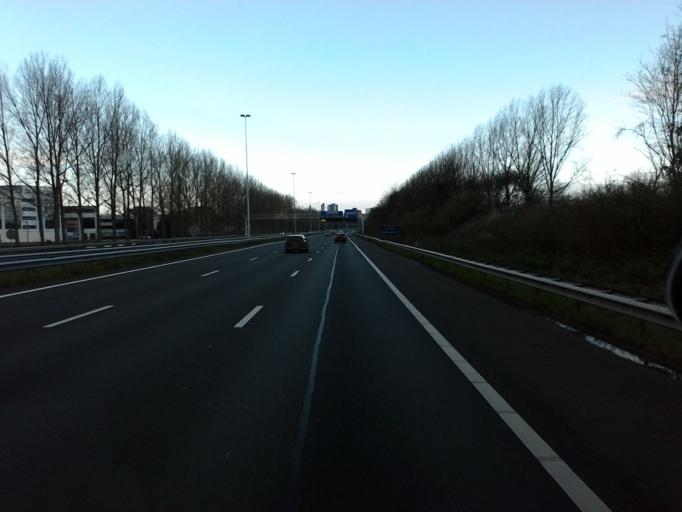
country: NL
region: South Holland
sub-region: Gemeente Capelle aan den IJssel
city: Capelle aan den IJssel
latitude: 51.9613
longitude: 4.5763
